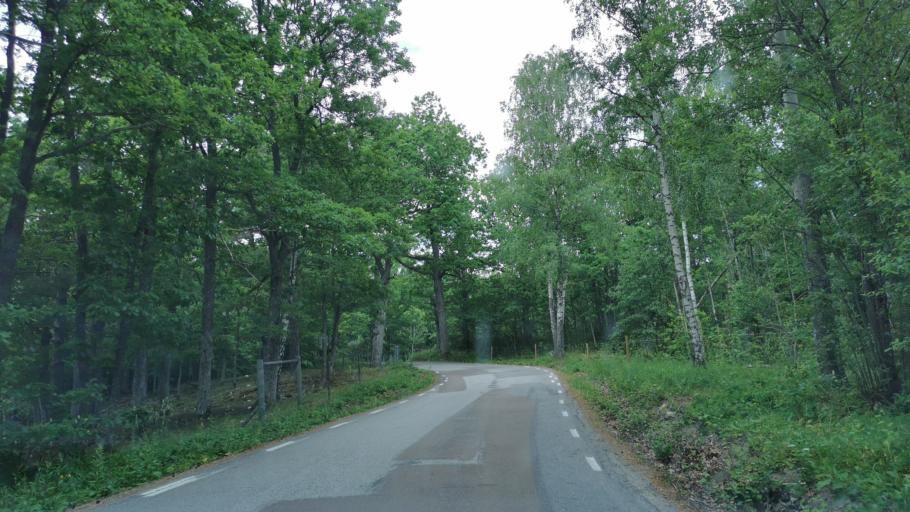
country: SE
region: Vaestra Goetaland
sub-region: Bengtsfors Kommun
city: Dals Langed
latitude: 58.8437
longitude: 12.4095
